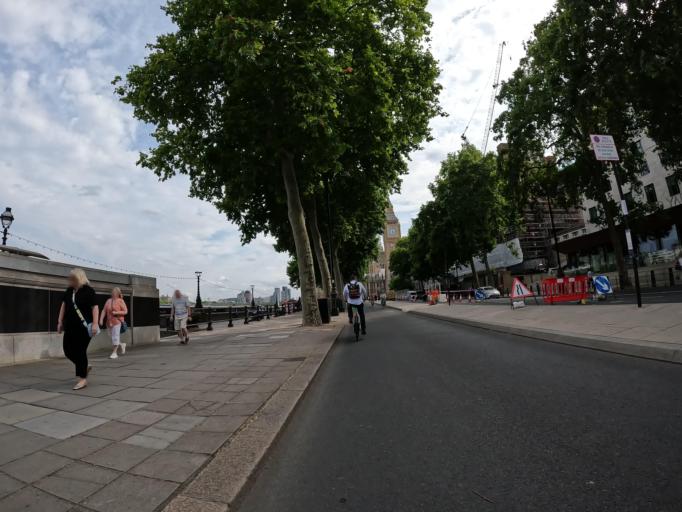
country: GB
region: England
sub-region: Greater London
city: Bromley
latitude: 51.3914
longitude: 0.0393
